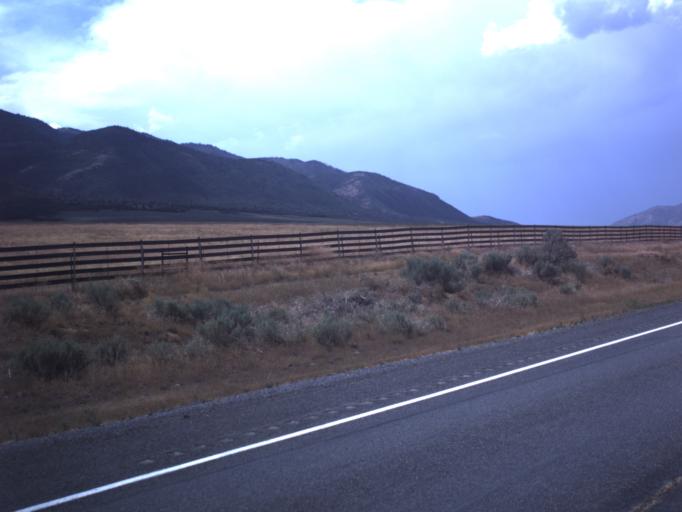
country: US
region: Utah
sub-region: Sanpete County
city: Fountain Green
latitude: 39.6702
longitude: -111.6628
